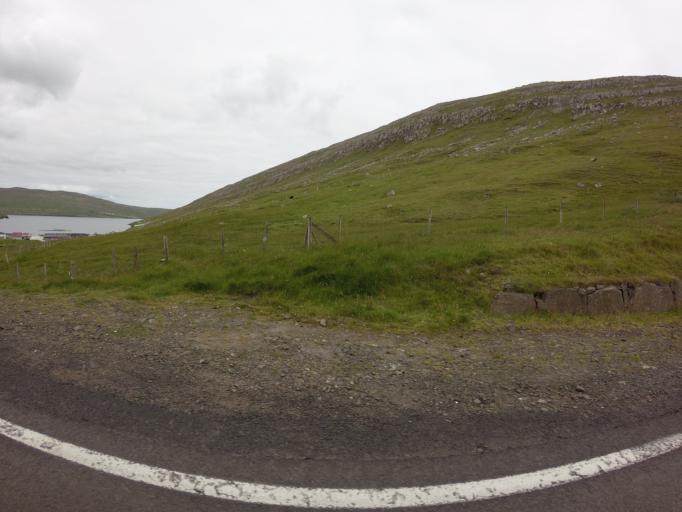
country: FO
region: Suduroy
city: Vagur
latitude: 61.4385
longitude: -6.7700
